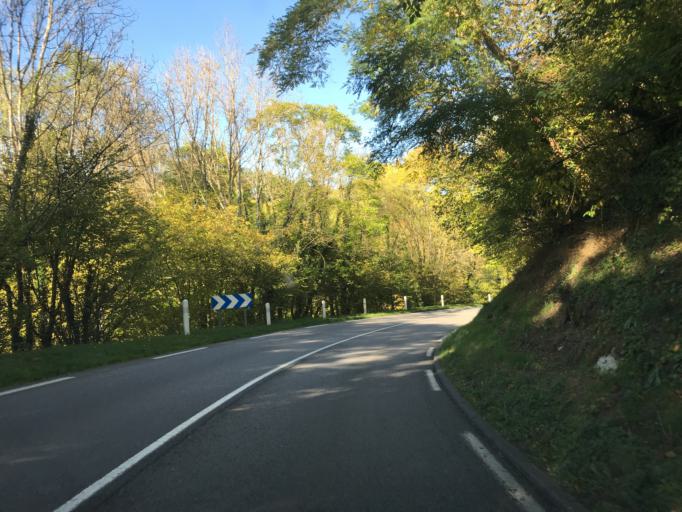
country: FR
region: Haute-Normandie
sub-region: Departement de l'Eure
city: Saint-Aubin-sur-Gaillon
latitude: 49.0850
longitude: 1.2634
